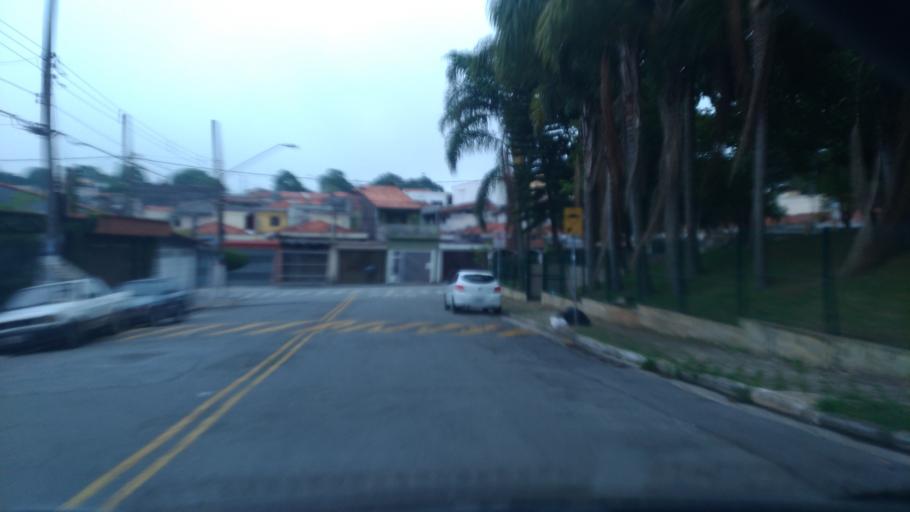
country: BR
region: Sao Paulo
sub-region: Sao Bernardo Do Campo
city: Sao Bernardo do Campo
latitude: -23.7189
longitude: -46.5712
